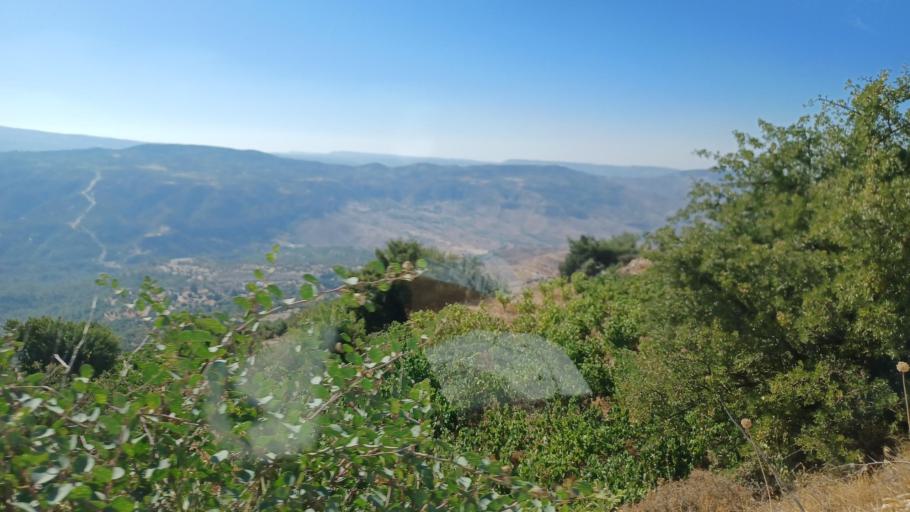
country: CY
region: Limassol
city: Pachna
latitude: 34.8996
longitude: 32.6436
